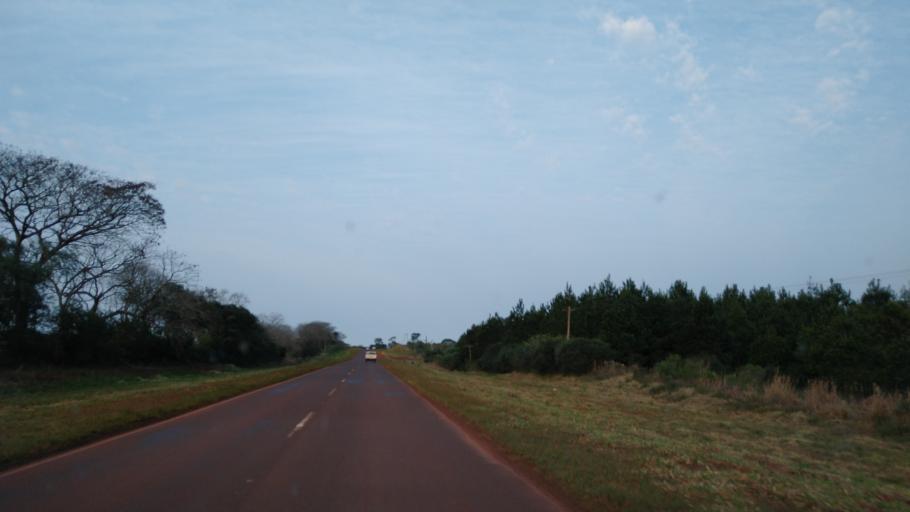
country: AR
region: Corrientes
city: San Carlos
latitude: -27.7515
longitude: -55.8786
